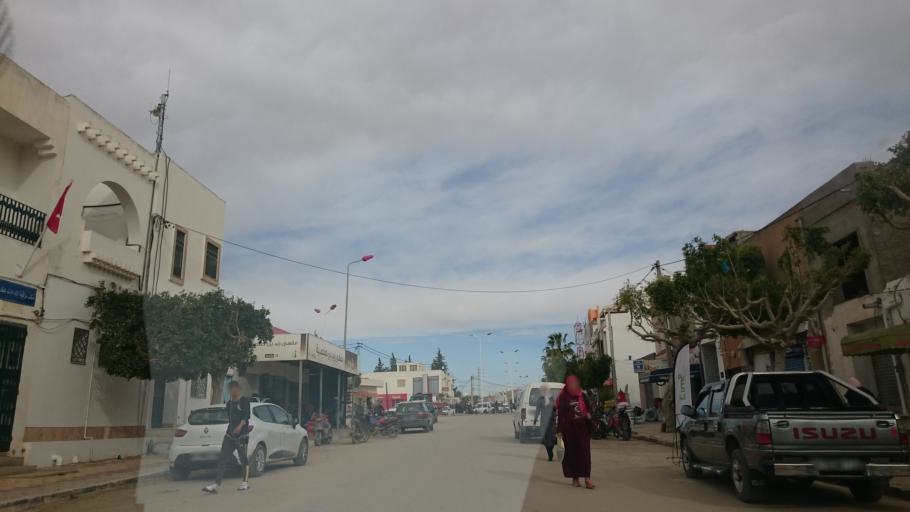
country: TN
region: Safaqis
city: Sfax
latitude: 34.7409
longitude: 10.5290
